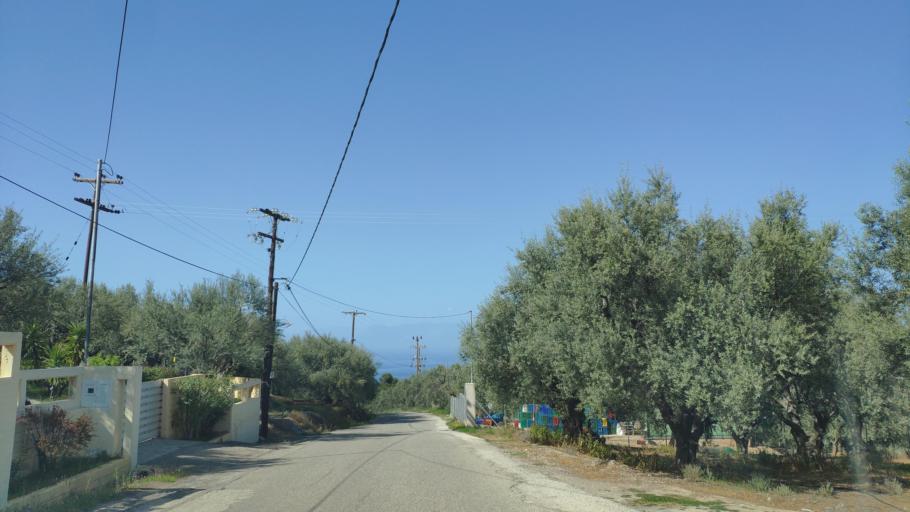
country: GR
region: West Greece
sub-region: Nomos Achaias
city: Aiyira
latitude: 38.1333
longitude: 22.3479
